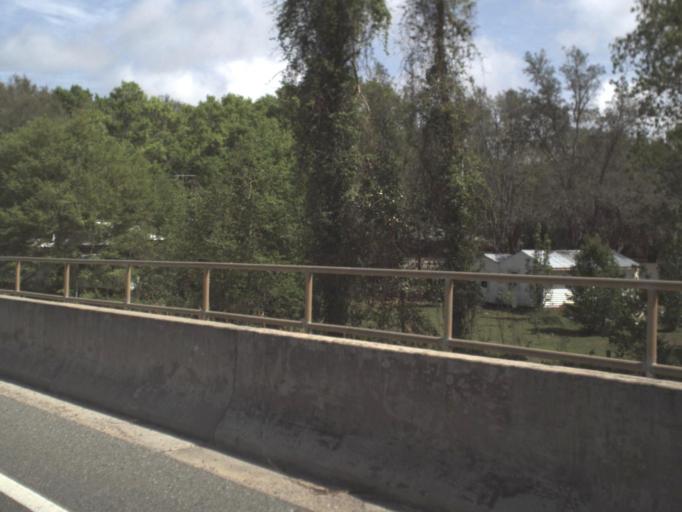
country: US
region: Florida
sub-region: Santa Rosa County
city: Navarre
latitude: 30.4420
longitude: -86.8665
